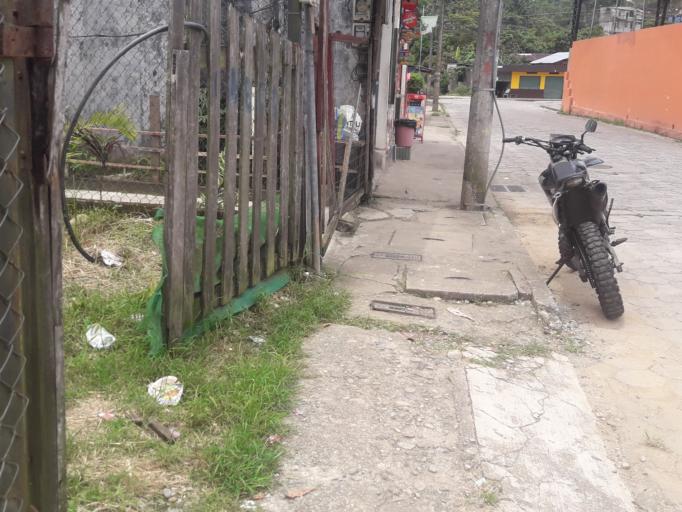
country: EC
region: Napo
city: Tena
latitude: -0.9935
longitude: -77.8089
